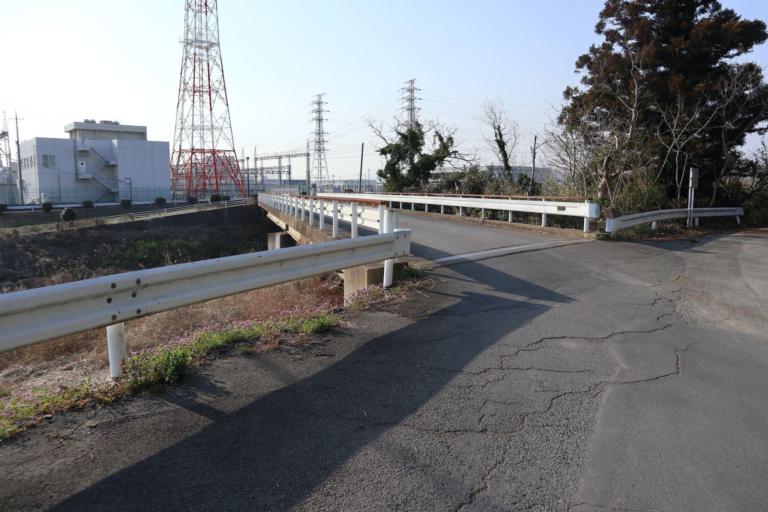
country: JP
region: Gunma
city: Tatebayashi
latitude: 36.2802
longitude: 139.5566
